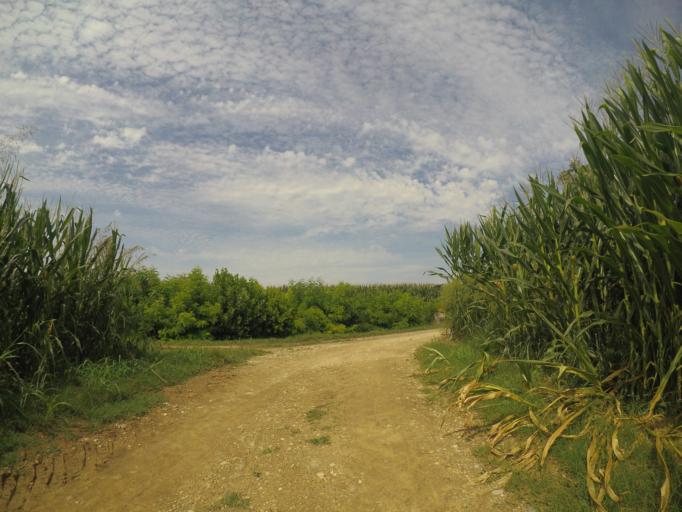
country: IT
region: Friuli Venezia Giulia
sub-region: Provincia di Udine
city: Bertiolo
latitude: 45.9333
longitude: 13.0677
